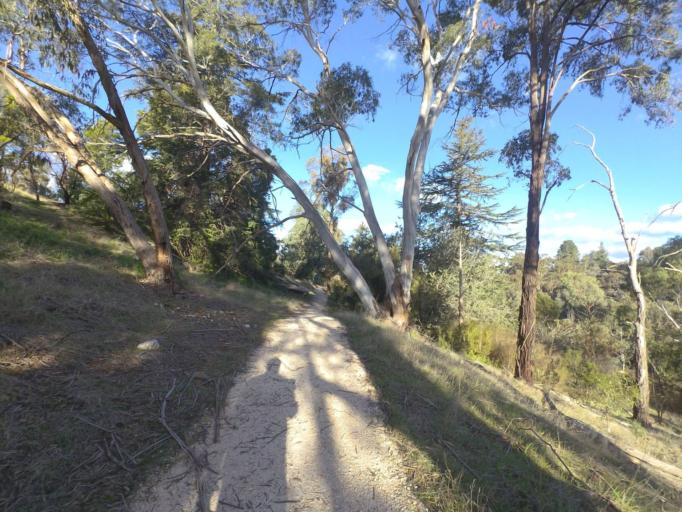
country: AU
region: Victoria
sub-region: Mount Alexander
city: Castlemaine
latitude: -37.1614
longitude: 144.2152
